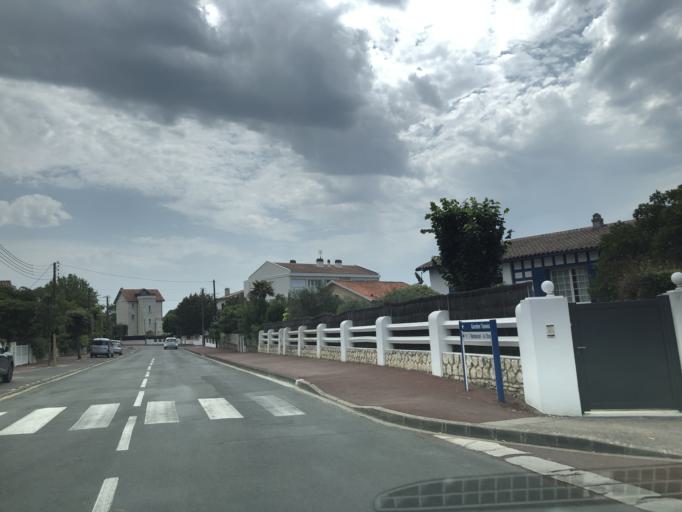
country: FR
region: Poitou-Charentes
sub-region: Departement de la Charente-Maritime
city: Royan
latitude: 45.6236
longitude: -1.0454
